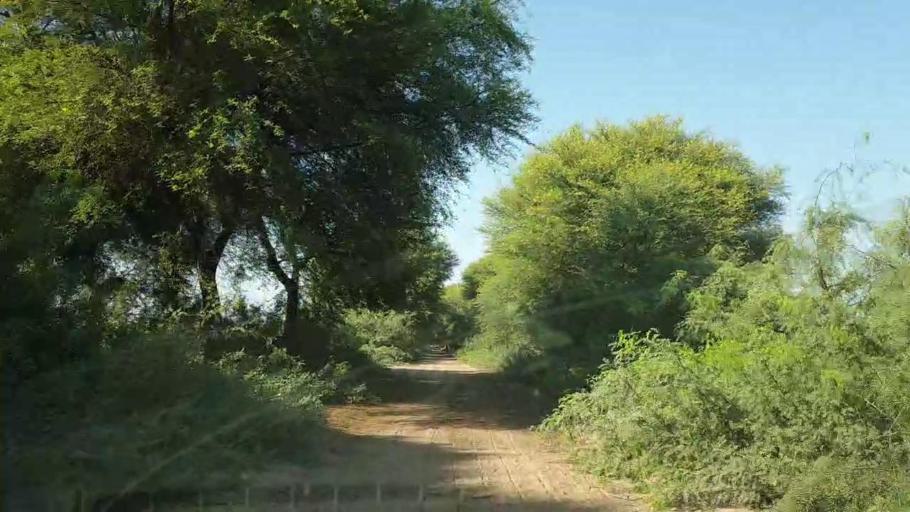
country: PK
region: Sindh
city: Tando Jam
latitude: 25.3548
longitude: 68.5699
